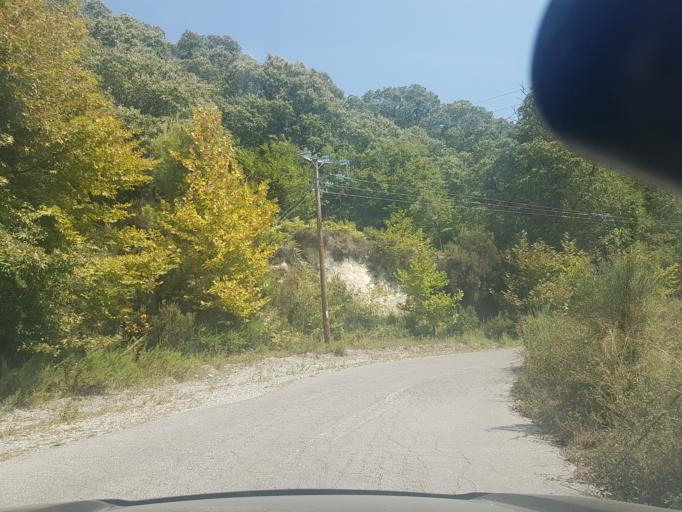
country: GR
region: Central Greece
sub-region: Nomos Evvoias
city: Yimnon
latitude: 38.6267
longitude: 23.8934
